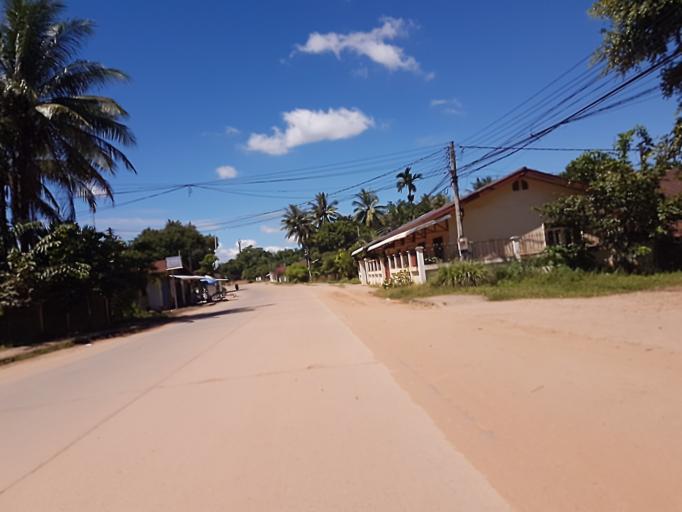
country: LA
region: Vientiane
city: Vientiane
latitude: 17.9211
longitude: 102.6297
